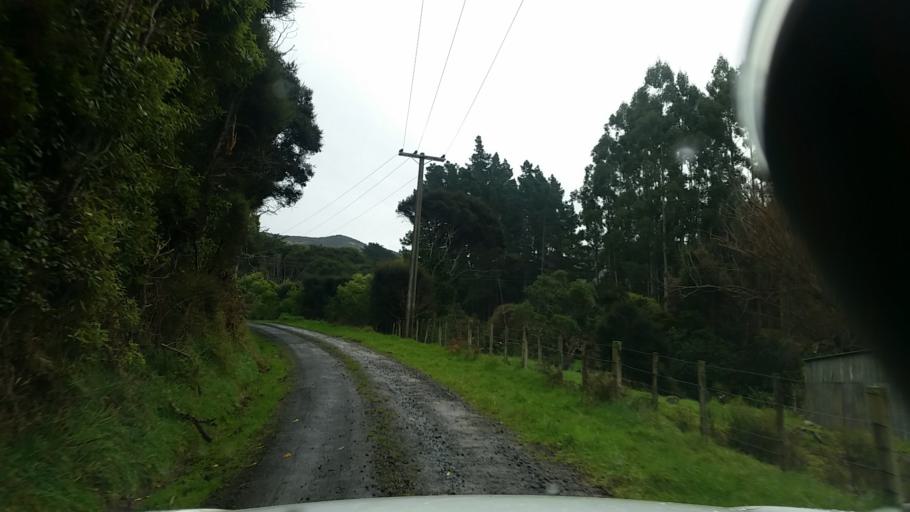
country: NZ
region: Canterbury
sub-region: Christchurch City
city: Christchurch
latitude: -43.7600
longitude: 173.0544
